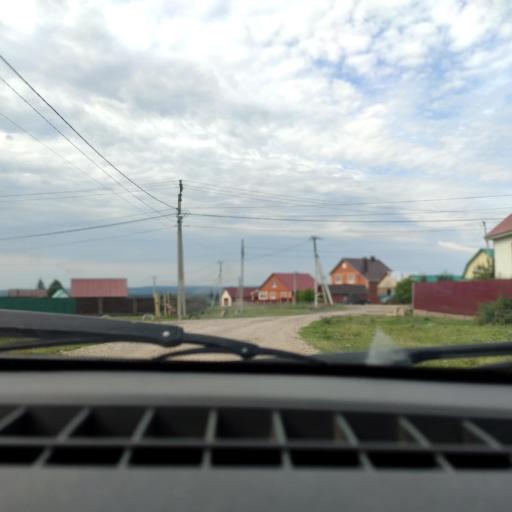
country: RU
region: Bashkortostan
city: Avdon
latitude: 54.6580
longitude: 55.7770
